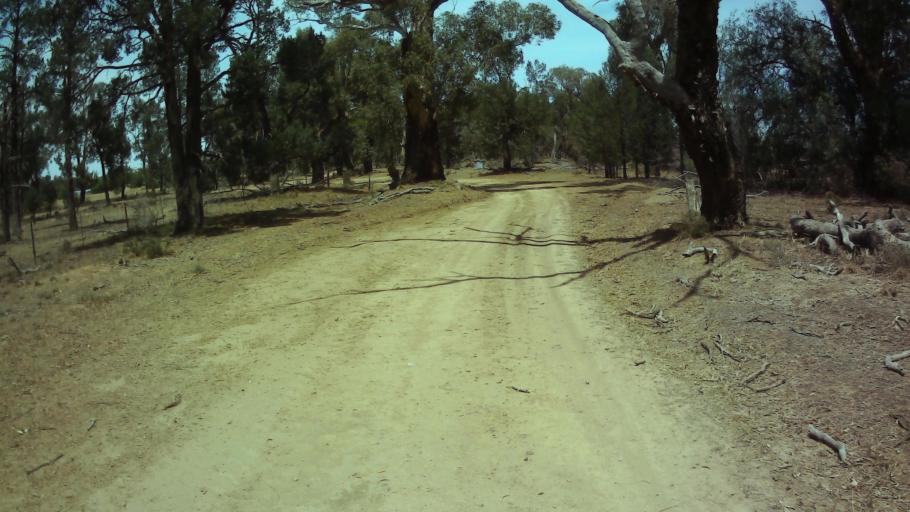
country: AU
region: New South Wales
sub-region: Weddin
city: Grenfell
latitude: -34.0311
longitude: 147.9334
